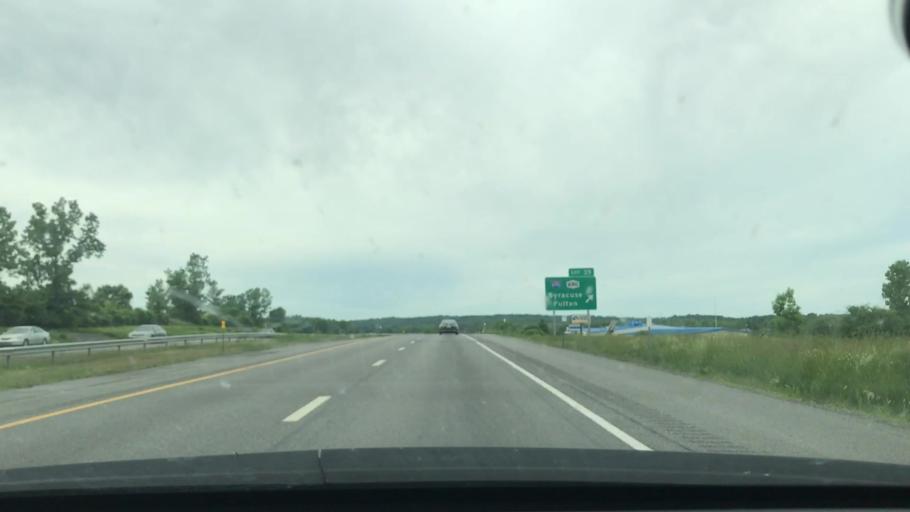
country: US
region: New York
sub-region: Onondaga County
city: Seneca Knolls
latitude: 43.1092
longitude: -76.2784
